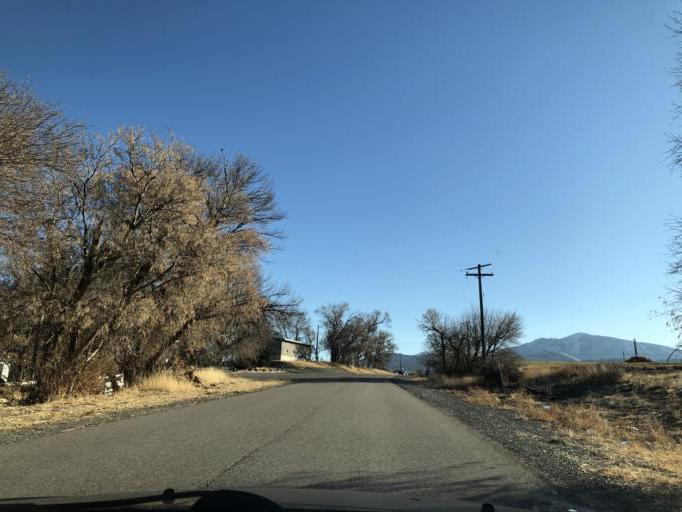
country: US
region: Utah
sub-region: Cache County
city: Wellsville
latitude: 41.6090
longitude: -111.9302
